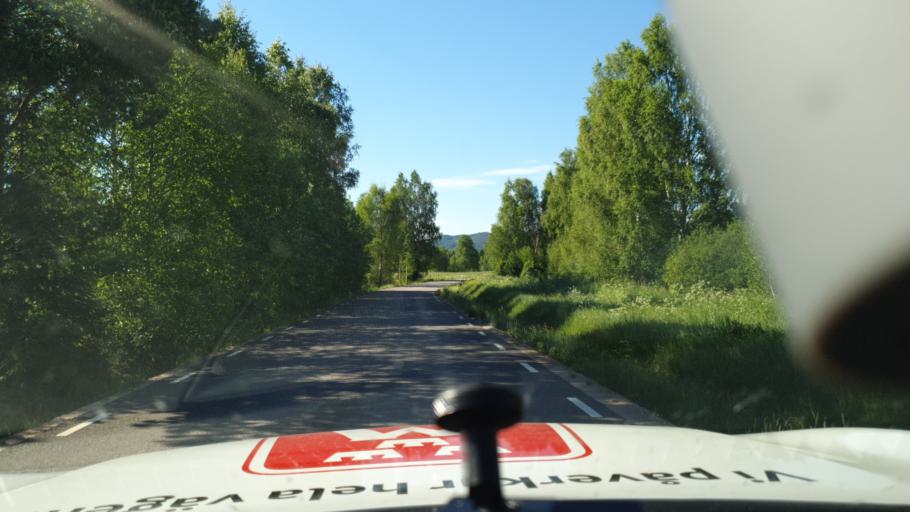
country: SE
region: Vaermland
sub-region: Torsby Kommun
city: Torsby
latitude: 60.2102
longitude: 13.0281
